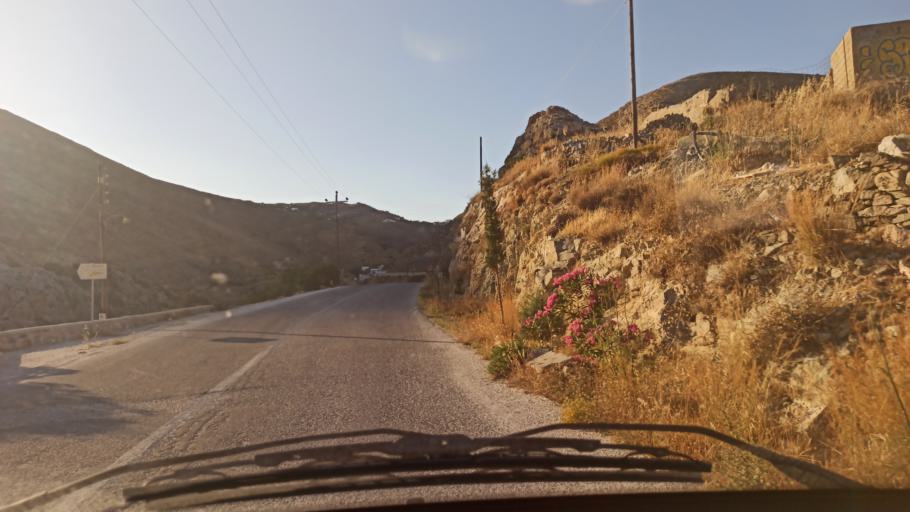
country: GR
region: South Aegean
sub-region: Nomos Kykladon
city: Ano Syros
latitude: 37.4534
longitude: 24.9340
